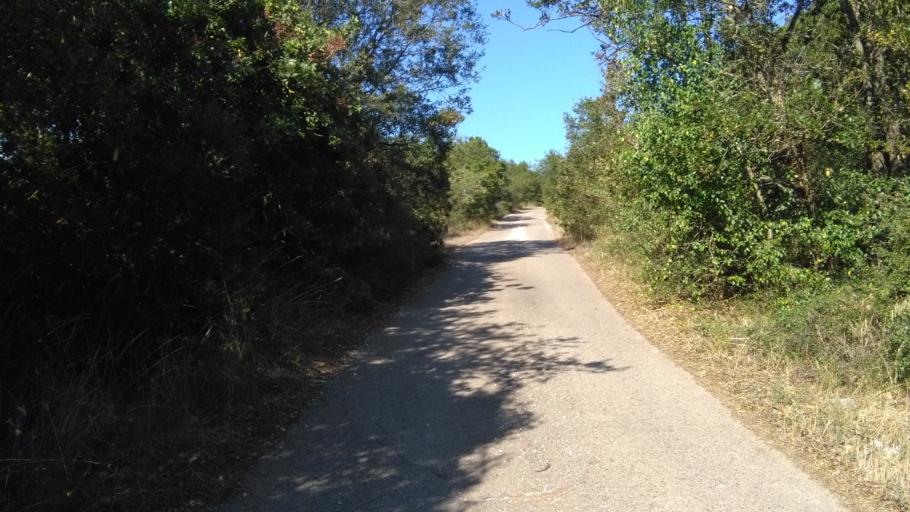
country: IT
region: Apulia
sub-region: Provincia di Bari
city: Putignano
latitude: 40.8195
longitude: 17.0349
